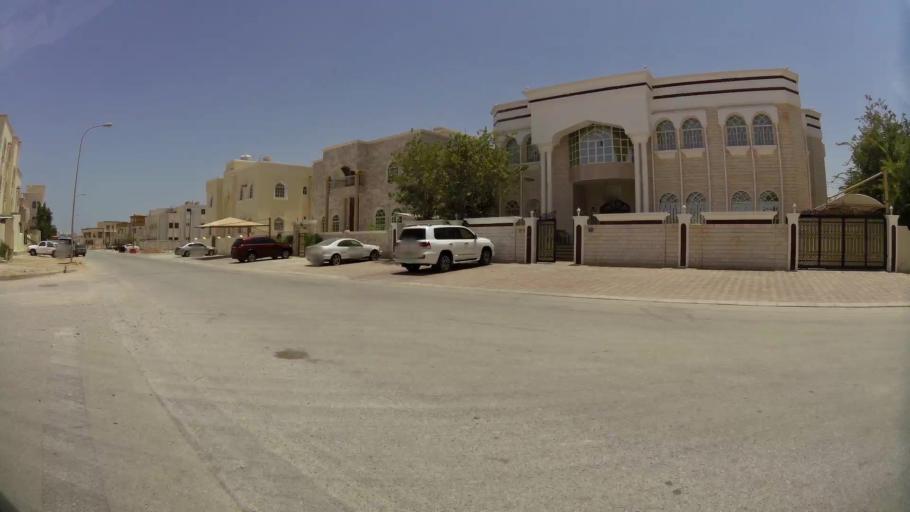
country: OM
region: Zufar
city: Salalah
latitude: 17.0752
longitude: 54.1504
